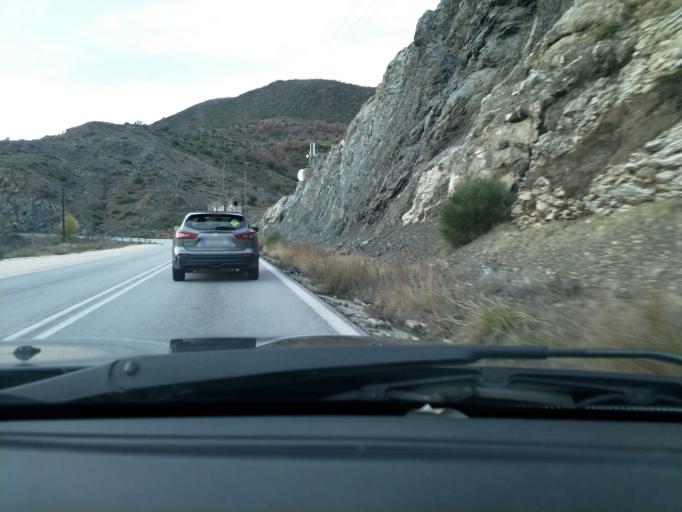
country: GR
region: Thessaly
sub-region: Trikala
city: Kastraki
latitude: 39.7556
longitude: 21.4999
